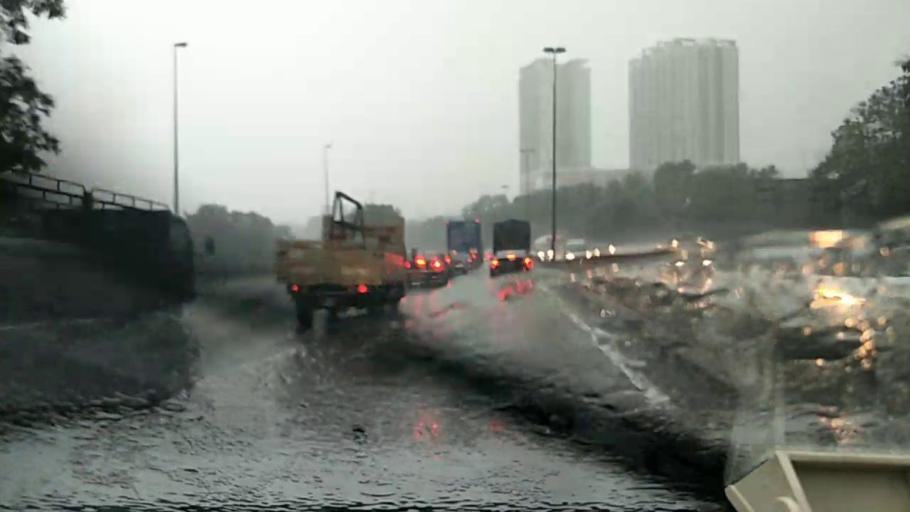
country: MY
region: Selangor
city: Kampong Baharu Balakong
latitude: 2.9808
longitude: 101.7350
